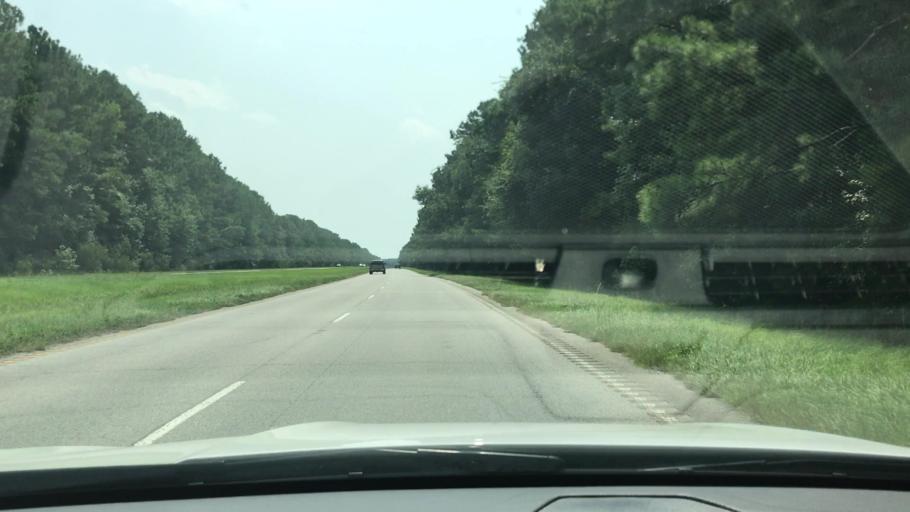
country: US
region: South Carolina
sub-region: Charleston County
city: Awendaw
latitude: 32.9718
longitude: -79.6747
